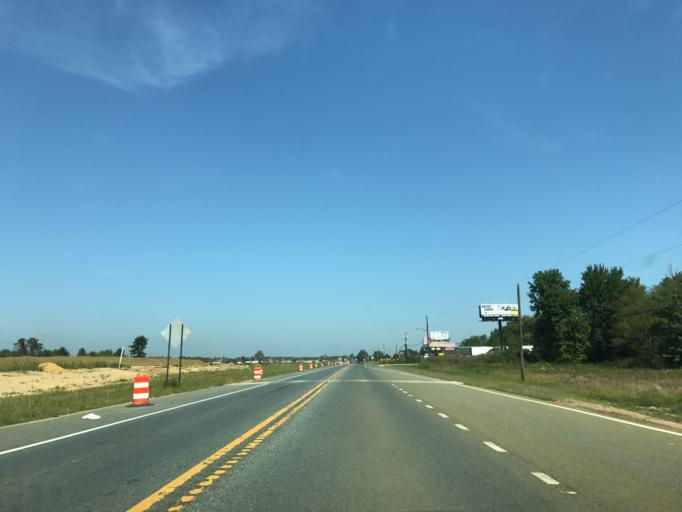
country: US
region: Delaware
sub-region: New Castle County
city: Middletown
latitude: 39.4214
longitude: -75.7635
